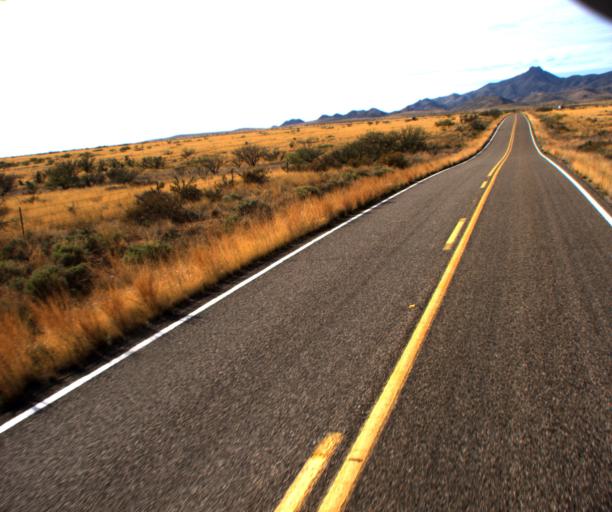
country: US
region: Arizona
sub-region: Cochise County
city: Willcox
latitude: 32.1089
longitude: -109.5480
